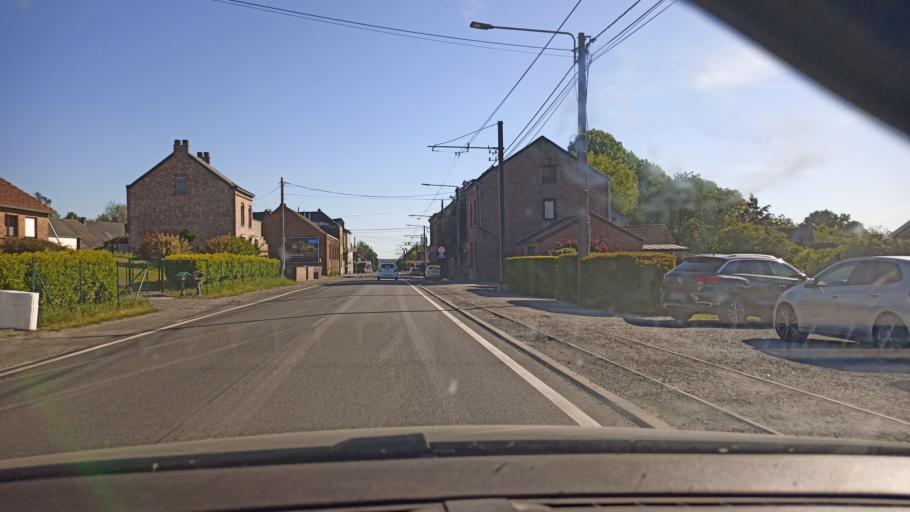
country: BE
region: Wallonia
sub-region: Province du Hainaut
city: Lobbes
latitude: 50.3592
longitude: 4.2714
